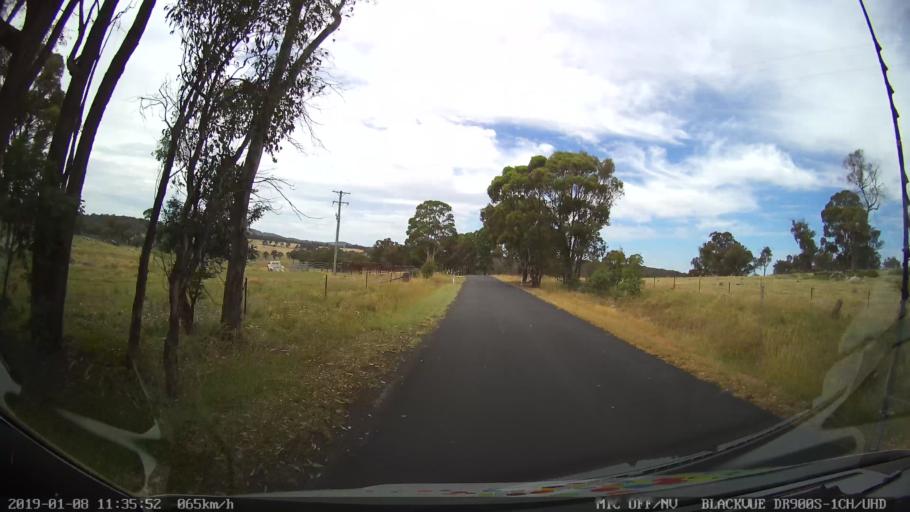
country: AU
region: New South Wales
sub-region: Guyra
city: Guyra
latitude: -30.3413
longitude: 151.5393
